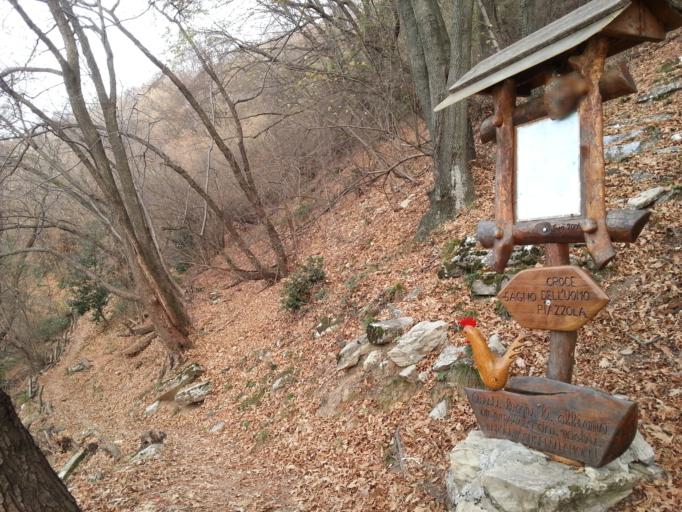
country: IT
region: Lombardy
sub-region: Provincia di Como
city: Maslianico
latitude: 45.8533
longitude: 9.0516
